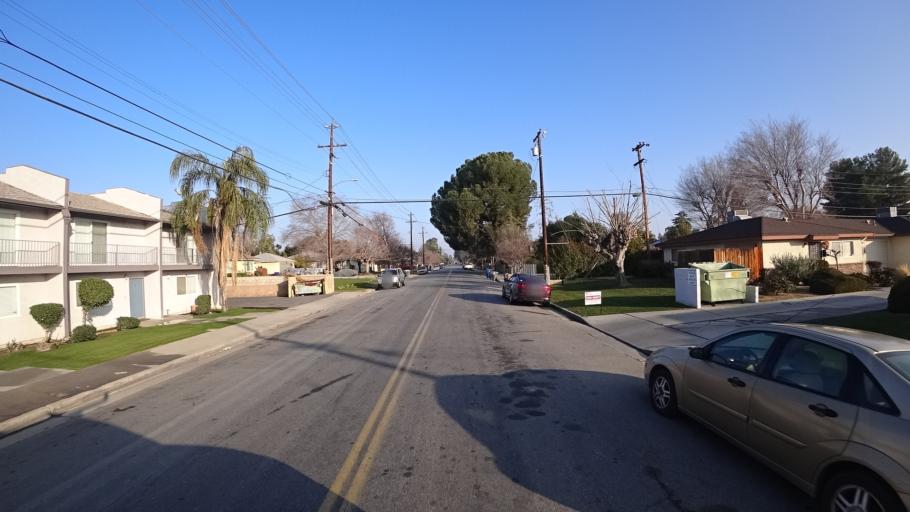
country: US
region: California
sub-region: Kern County
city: Bakersfield
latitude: 35.3559
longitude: -119.0459
